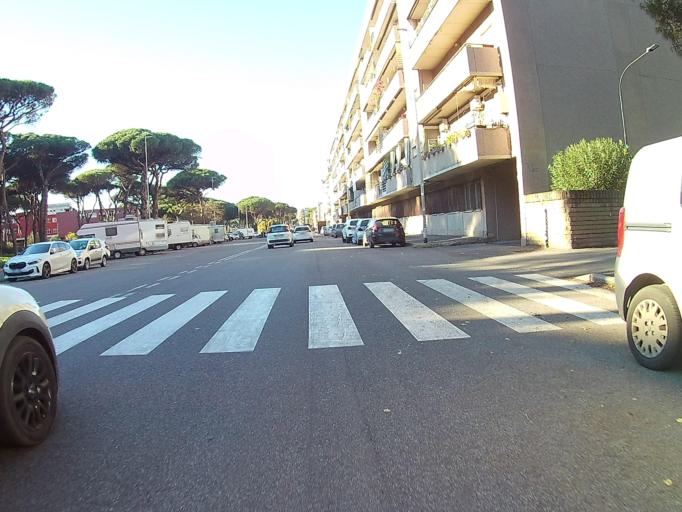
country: IT
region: Latium
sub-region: Citta metropolitana di Roma Capitale
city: Lido di Ostia
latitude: 41.7341
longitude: 12.2975
